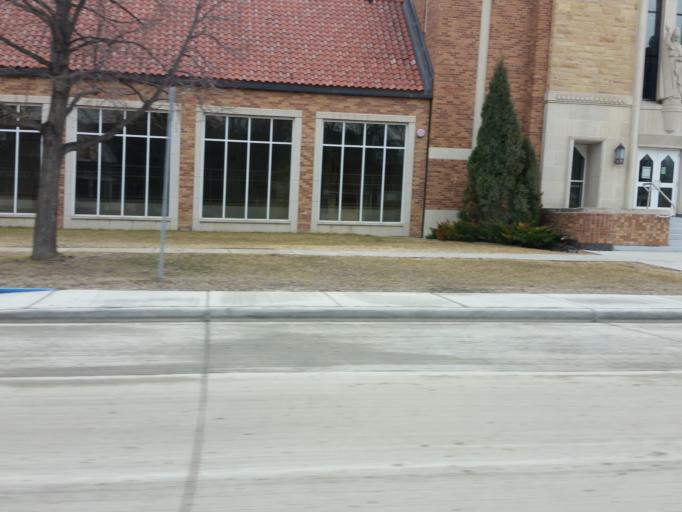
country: US
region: North Dakota
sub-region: Cass County
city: Casselton
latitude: 46.9031
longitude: -97.2111
